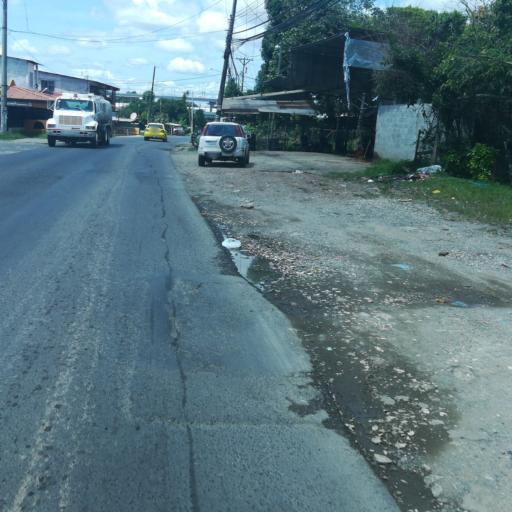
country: PA
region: Panama
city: Tocumen
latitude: 9.0837
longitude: -79.3947
